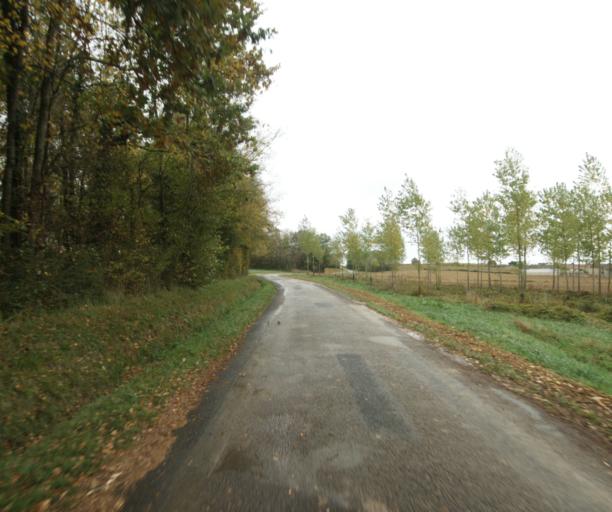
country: FR
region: Bourgogne
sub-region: Departement de Saone-et-Loire
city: Saint-Martin-Belle-Roche
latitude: 46.4779
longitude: 4.8509
